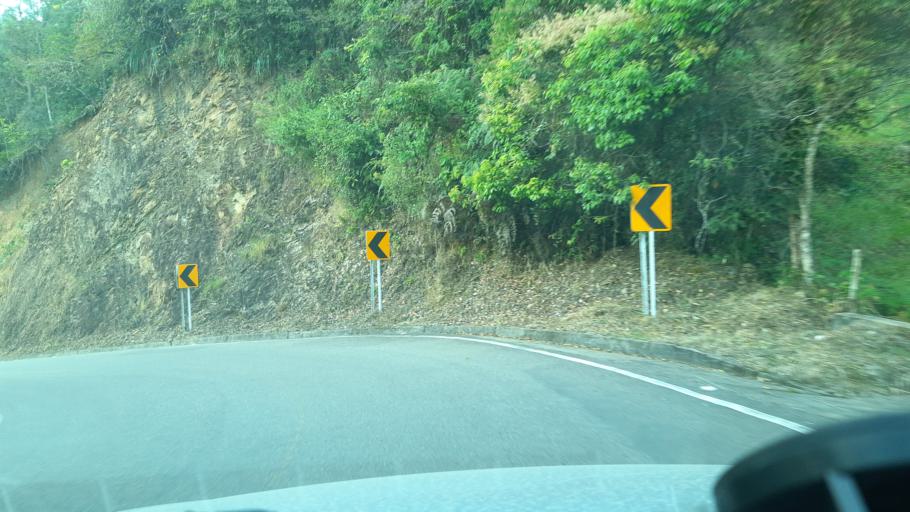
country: CO
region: Boyaca
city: Chivor
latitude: 4.9749
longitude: -73.3284
